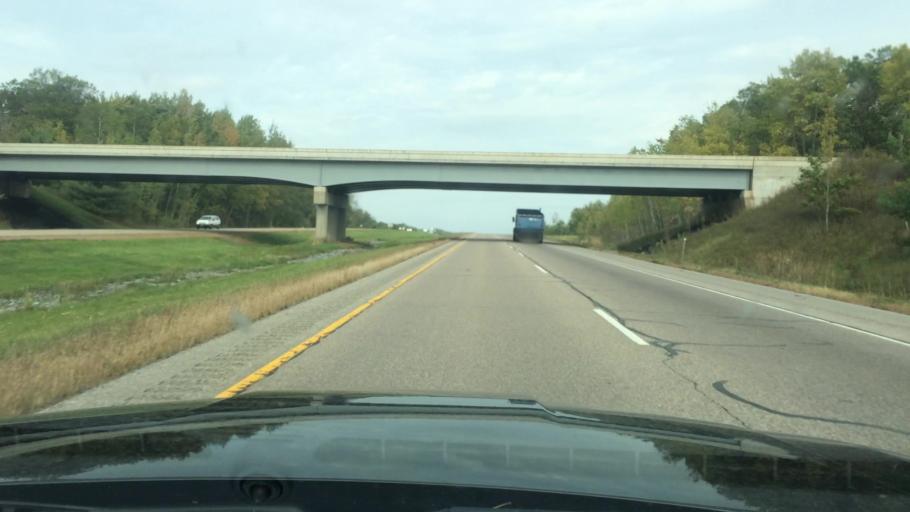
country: US
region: Wisconsin
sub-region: Marathon County
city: Mosinee
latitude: 44.6750
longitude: -89.6418
